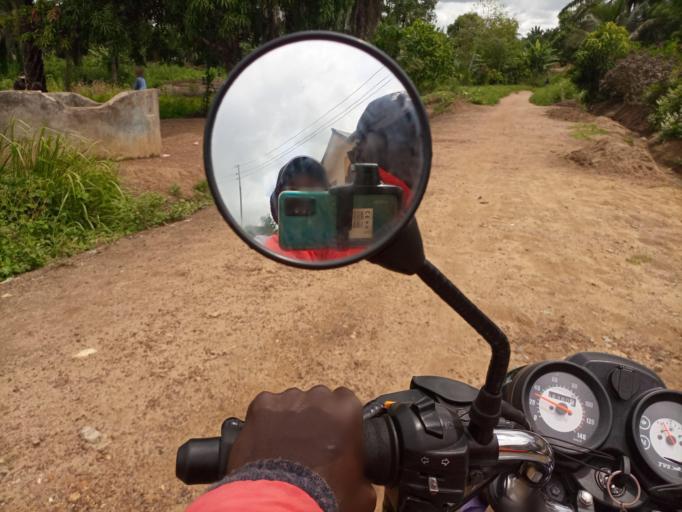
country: SL
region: Southern Province
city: Bo
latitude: 7.9735
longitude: -11.7230
